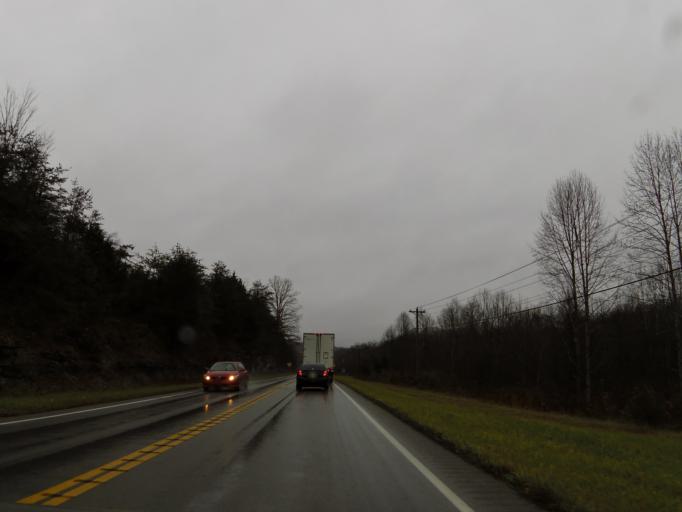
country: US
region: Kentucky
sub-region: Rockcastle County
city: Mount Vernon
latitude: 37.3950
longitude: -84.3337
